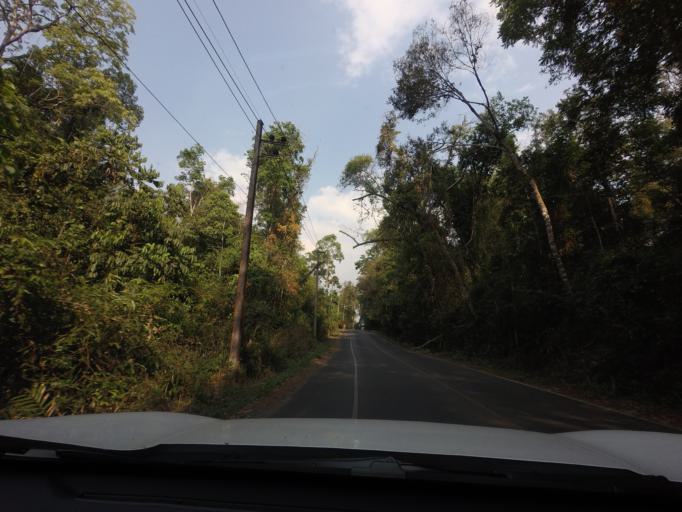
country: TH
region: Nakhon Ratchasima
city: Pak Chong
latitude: 14.4309
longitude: 101.3963
